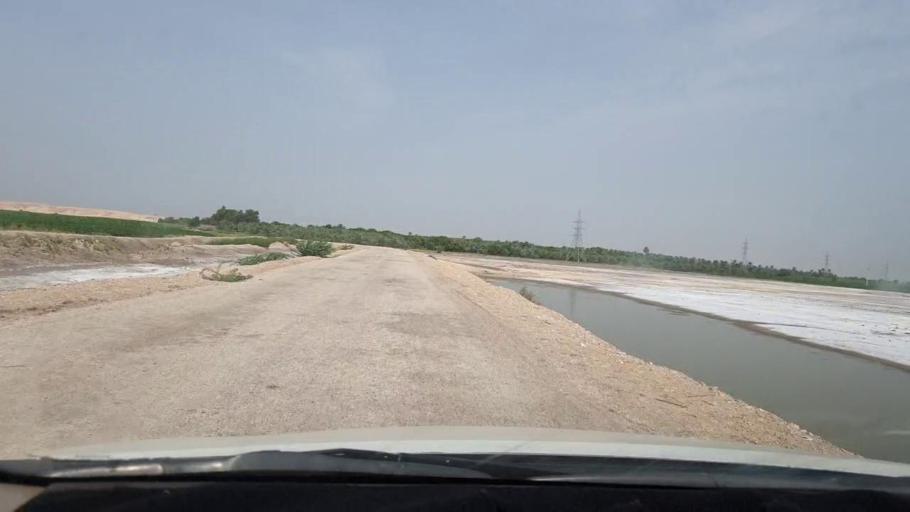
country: PK
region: Sindh
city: Rohri
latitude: 27.5959
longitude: 68.9869
